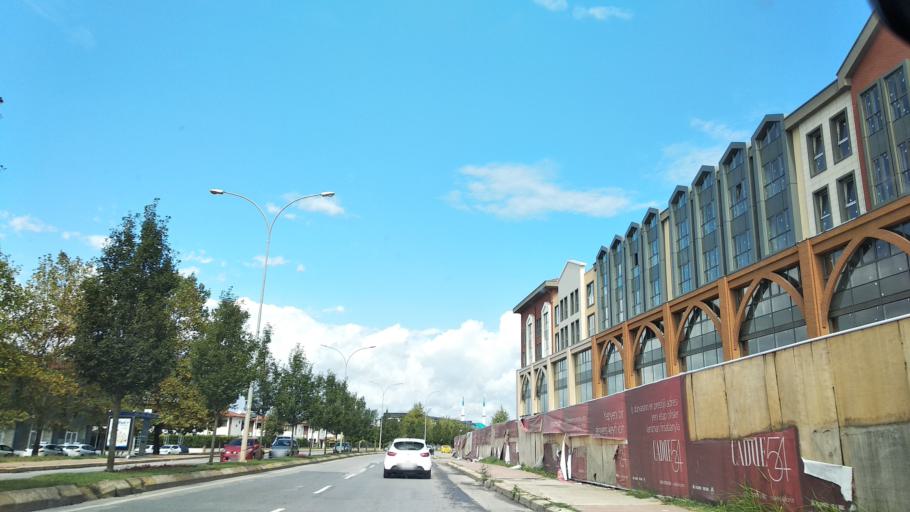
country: TR
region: Sakarya
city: Adapazari
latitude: 40.7749
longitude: 30.3640
